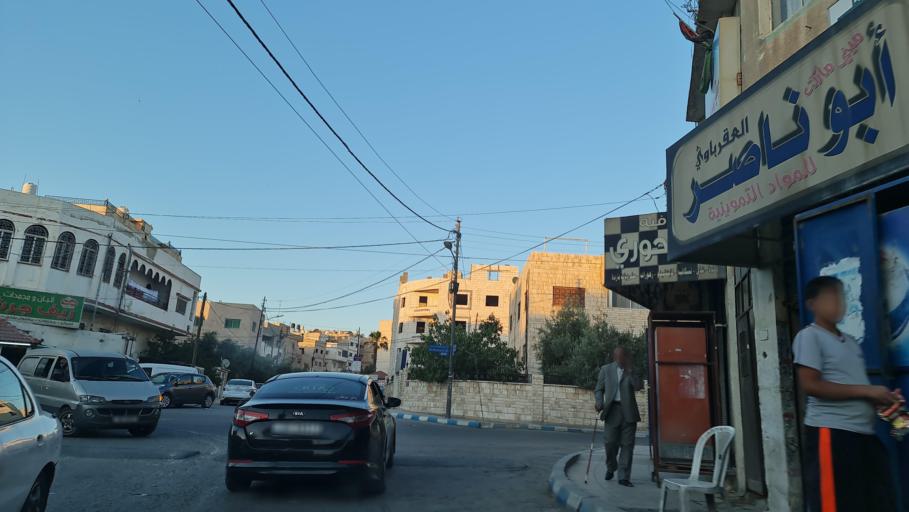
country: JO
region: Zarqa
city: Zarqa
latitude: 32.0770
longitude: 36.0805
